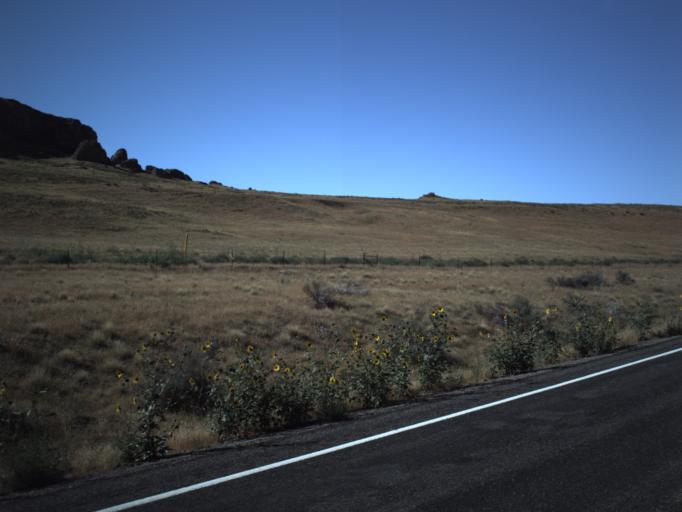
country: US
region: Utah
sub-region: Millard County
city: Delta
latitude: 39.6500
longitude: -112.2958
